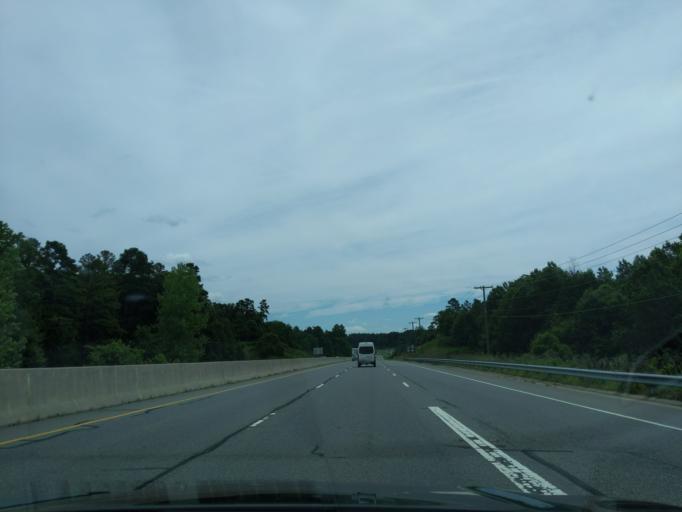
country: US
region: North Carolina
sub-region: Cabarrus County
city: Concord
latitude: 35.3743
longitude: -80.5459
